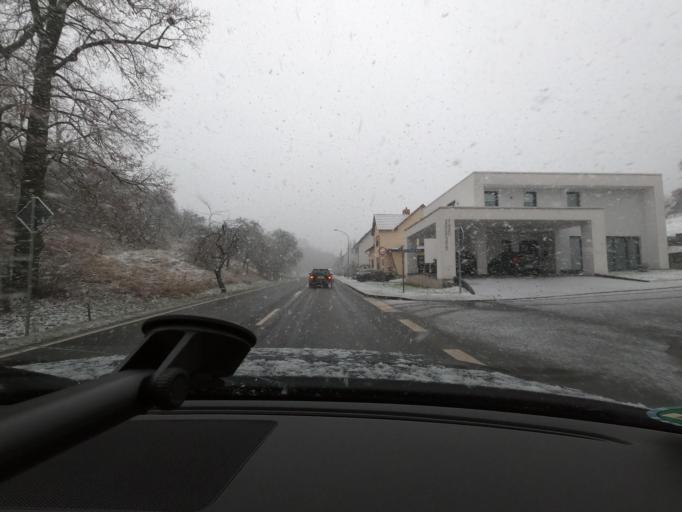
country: DE
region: Thuringia
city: Kallmerode
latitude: 51.3488
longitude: 10.3081
